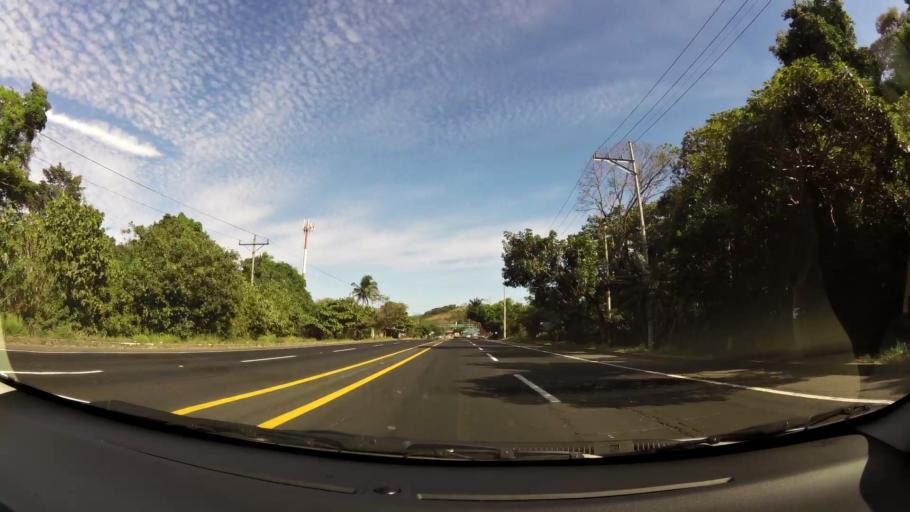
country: SV
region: Santa Ana
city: Santa Ana
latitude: 13.9853
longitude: -89.6006
